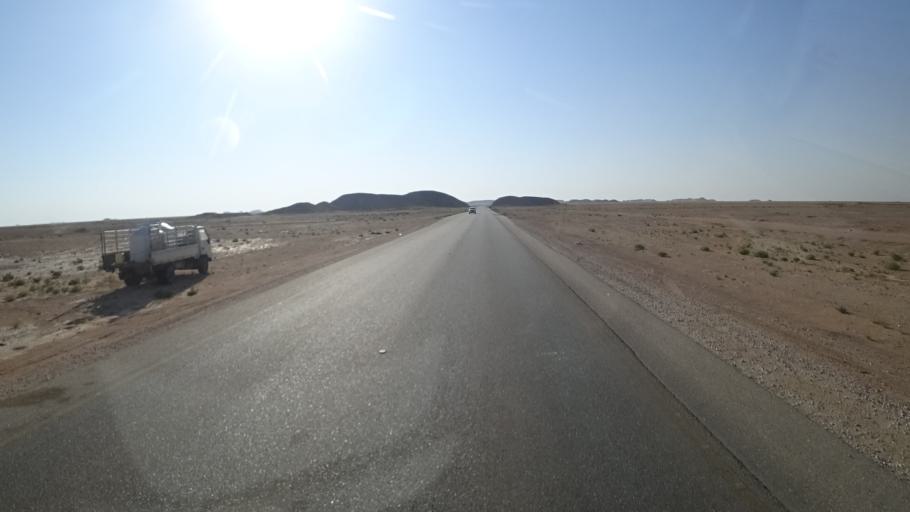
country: OM
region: Zufar
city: Salalah
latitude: 17.6396
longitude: 53.8948
